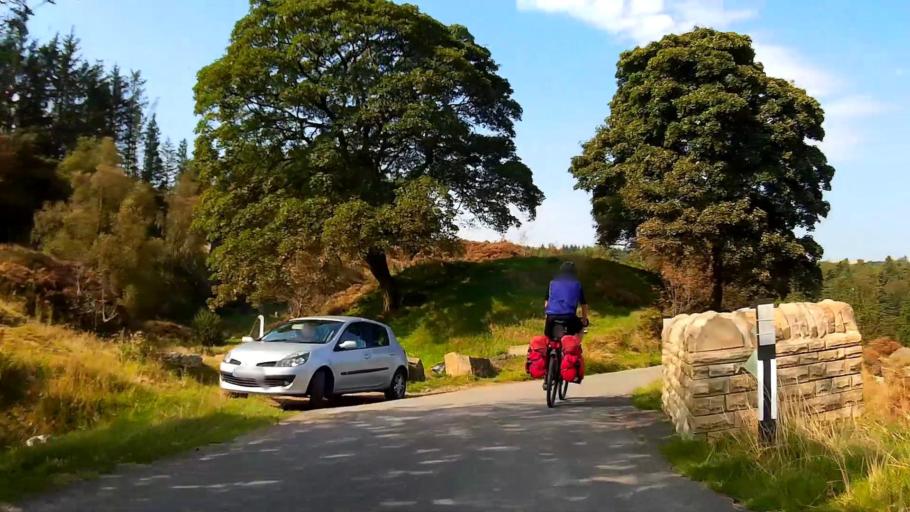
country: GB
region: England
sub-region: Derbyshire
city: Buxton
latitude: 53.2565
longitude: -1.9828
